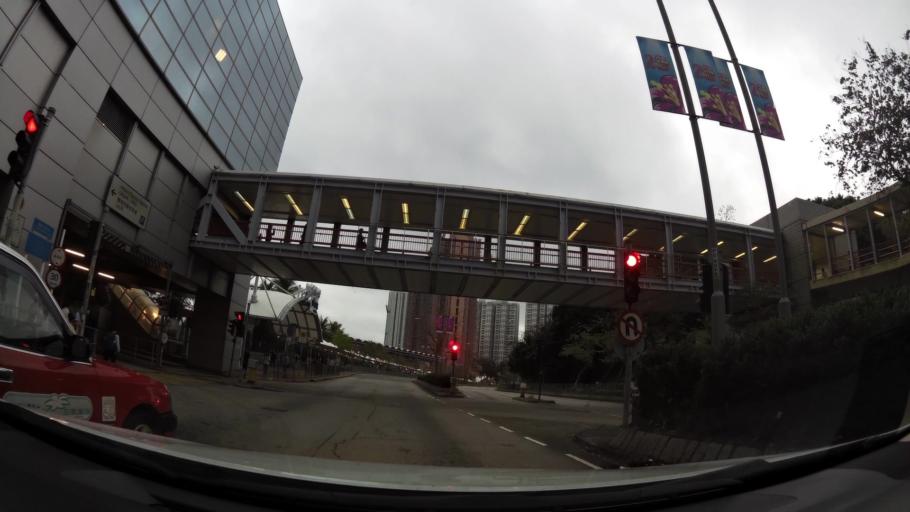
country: HK
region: Tsuen Wan
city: Tsuen Wan
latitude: 22.3576
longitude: 114.1063
